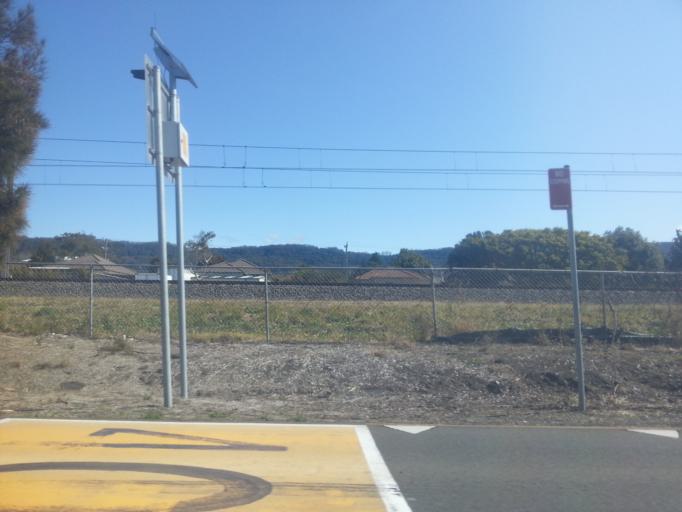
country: AU
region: New South Wales
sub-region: Wollongong
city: Bulli
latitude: -34.3531
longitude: 150.9141
